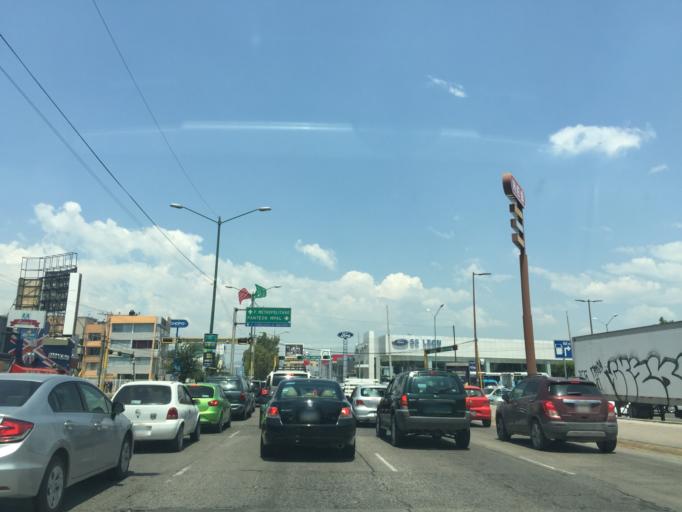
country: MX
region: Guanajuato
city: Leon
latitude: 21.1463
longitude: -101.6852
